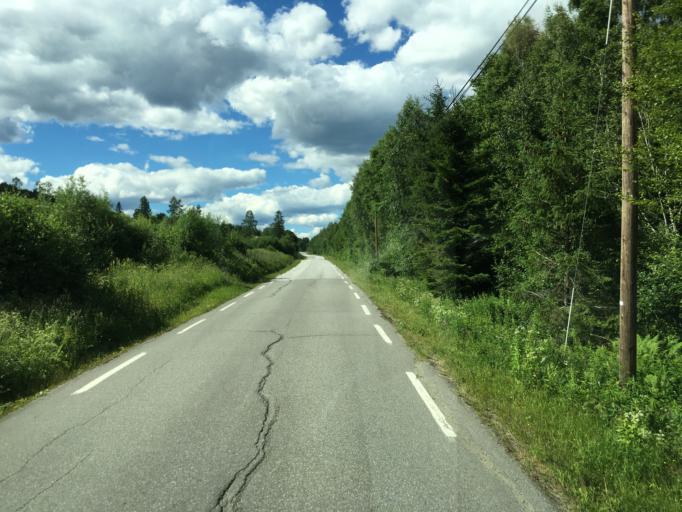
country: NO
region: Oppland
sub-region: Sondre Land
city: Hov
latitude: 60.6900
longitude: 10.3001
